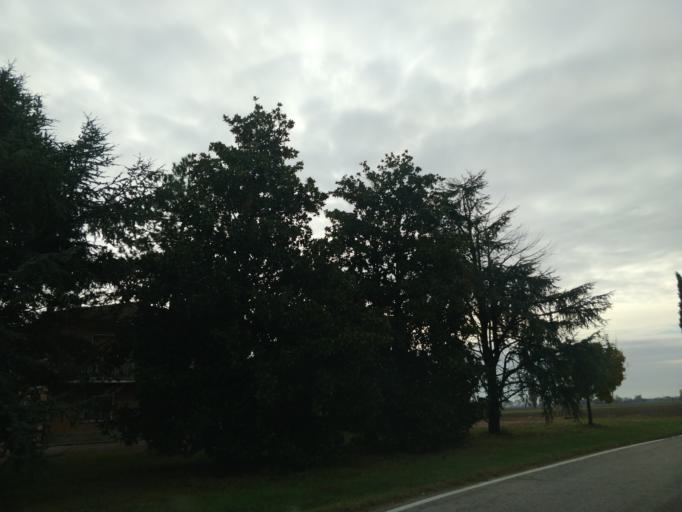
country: IT
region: Emilia-Romagna
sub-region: Provincia di Bologna
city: Argelato
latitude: 44.6368
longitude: 11.3249
